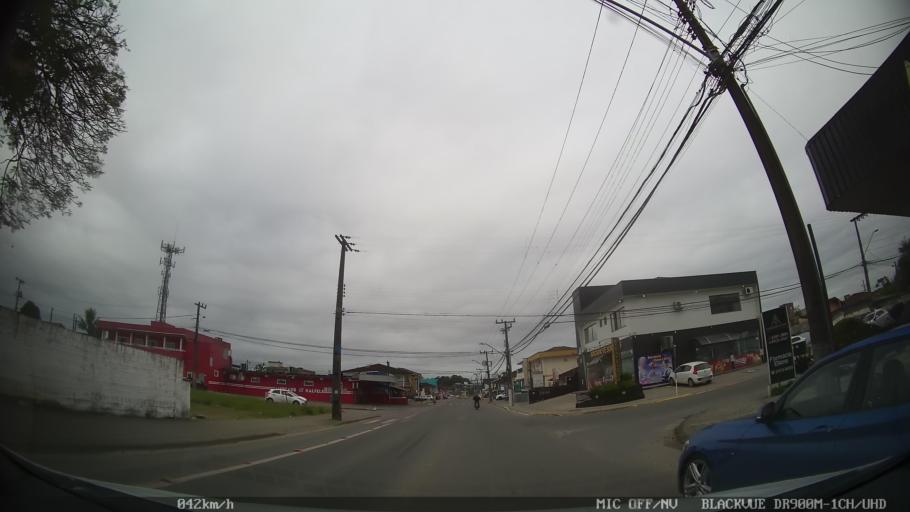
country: BR
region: Santa Catarina
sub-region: Joinville
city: Joinville
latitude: -26.2733
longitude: -48.8829
